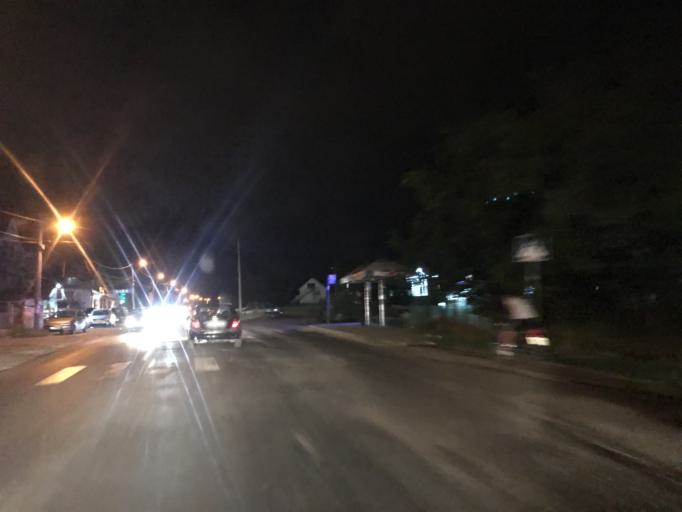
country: RS
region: Central Serbia
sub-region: Belgrade
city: Zvezdara
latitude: 44.7624
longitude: 20.5661
